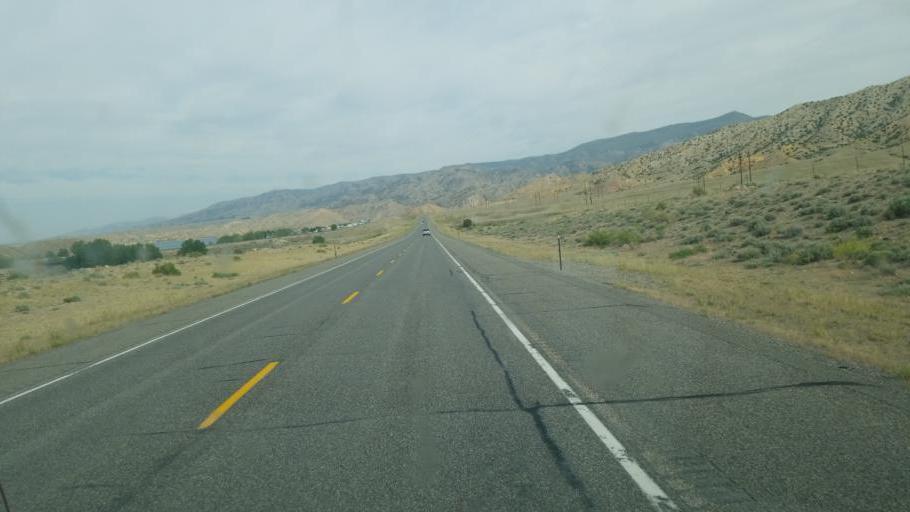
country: US
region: Wyoming
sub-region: Hot Springs County
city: Thermopolis
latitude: 43.3871
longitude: -108.1486
